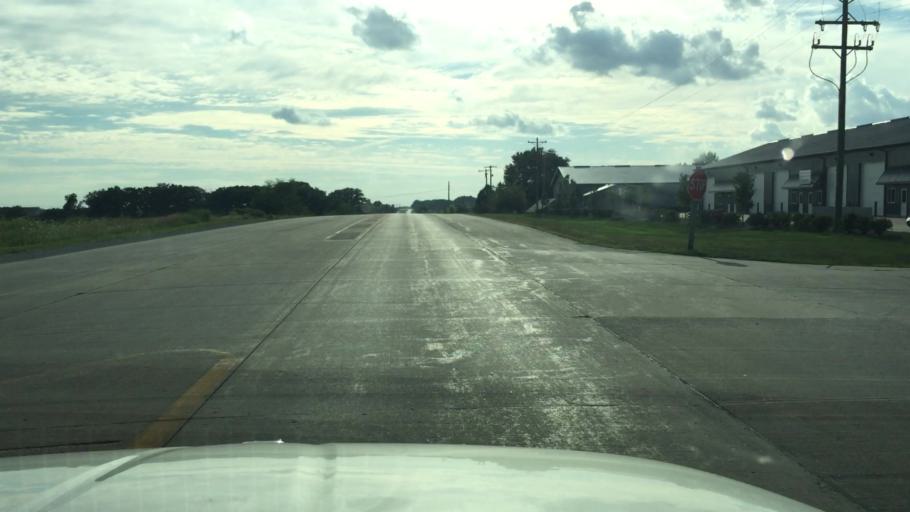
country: US
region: Iowa
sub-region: Johnson County
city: Iowa City
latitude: 41.6711
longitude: -91.4526
